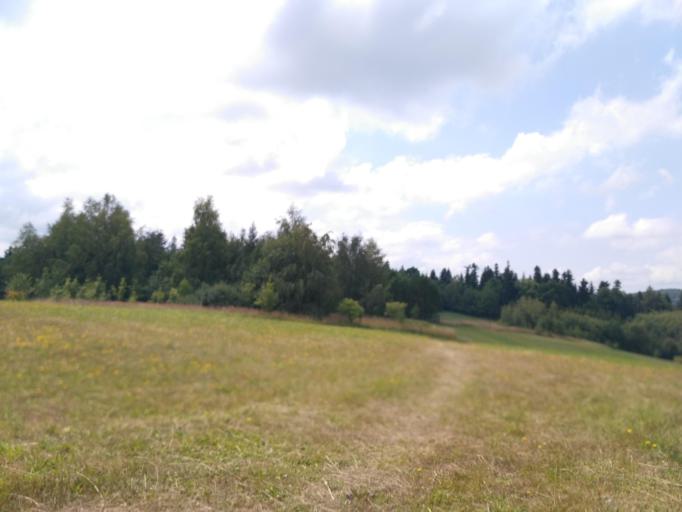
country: PL
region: Subcarpathian Voivodeship
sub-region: Powiat krosnienski
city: Iwonicz-Zdroj
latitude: 49.5765
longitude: 21.8068
